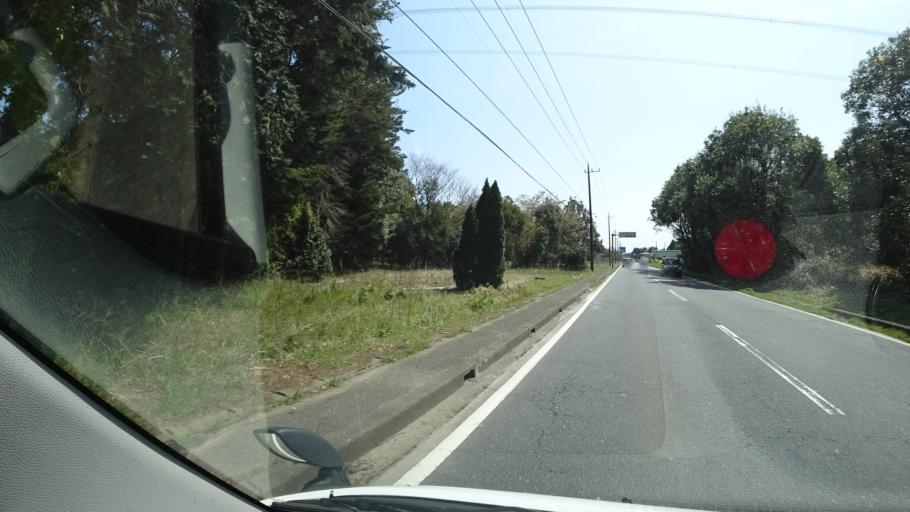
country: JP
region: Chiba
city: Naruto
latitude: 35.6735
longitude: 140.4320
